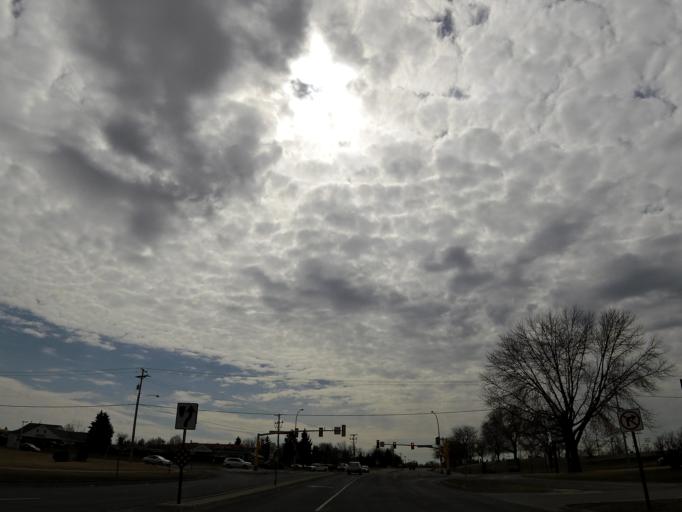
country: US
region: Minnesota
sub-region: Scott County
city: Savage
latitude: 44.8088
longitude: -93.3840
